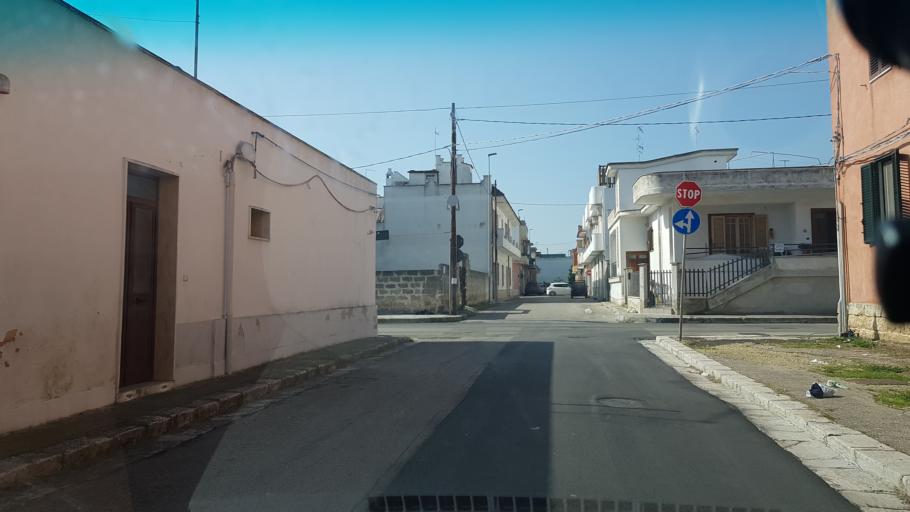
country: IT
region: Apulia
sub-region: Provincia di Brindisi
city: San Pietro Vernotico
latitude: 40.4824
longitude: 17.9988
